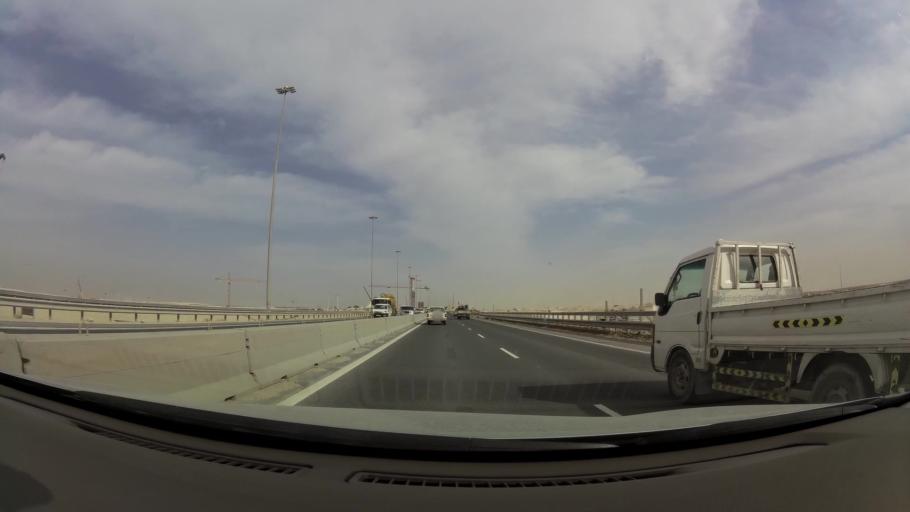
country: QA
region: Baladiyat ar Rayyan
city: Ash Shahaniyah
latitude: 25.3401
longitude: 51.3181
